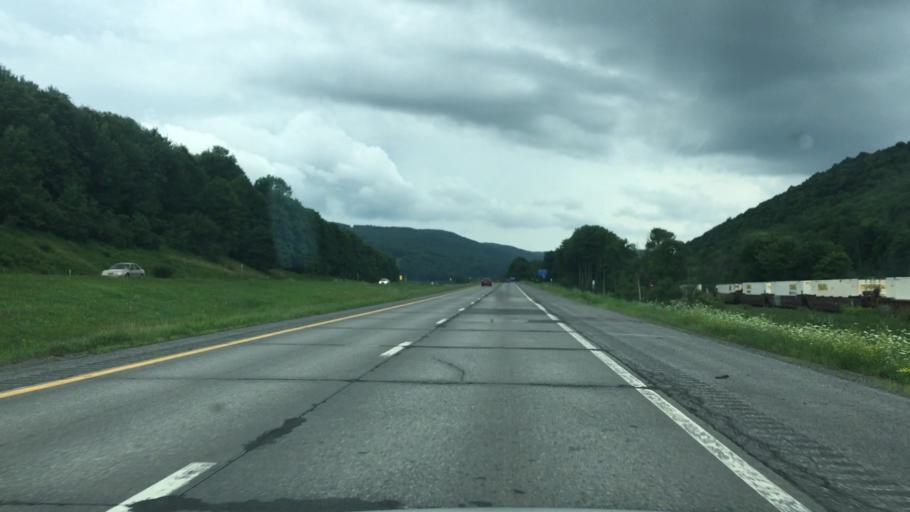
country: US
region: New York
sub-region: Otsego County
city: Worcester
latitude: 42.6357
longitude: -74.6554
